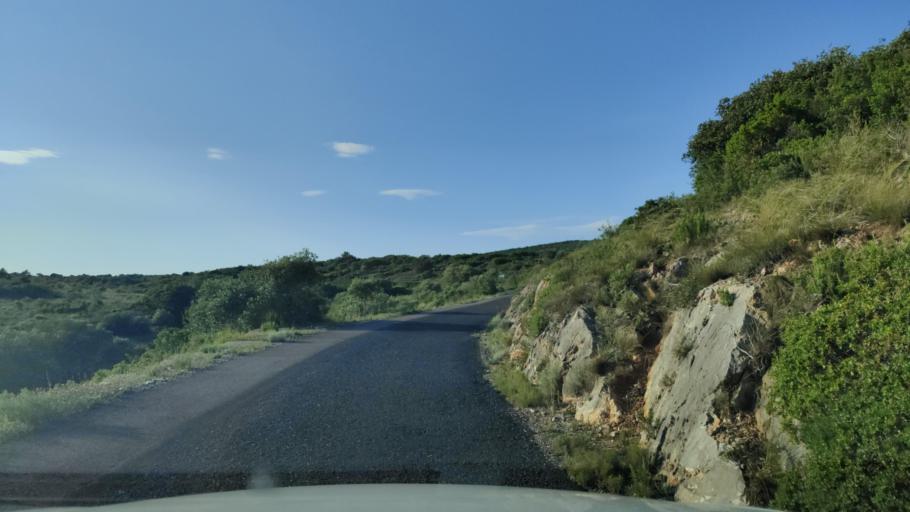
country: FR
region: Languedoc-Roussillon
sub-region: Departement des Pyrenees-Orientales
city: Estagel
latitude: 42.7868
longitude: 2.7443
